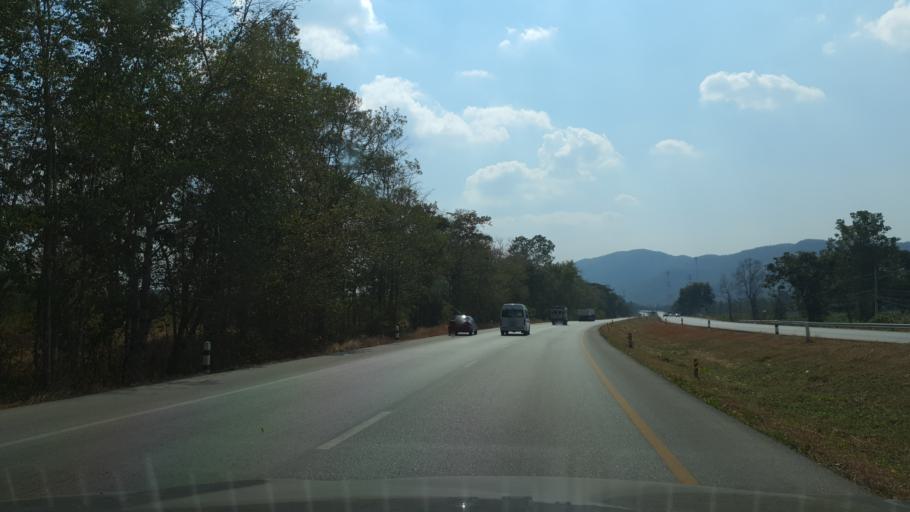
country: TH
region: Lampang
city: Mae Phrik
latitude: 17.3744
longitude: 99.1492
